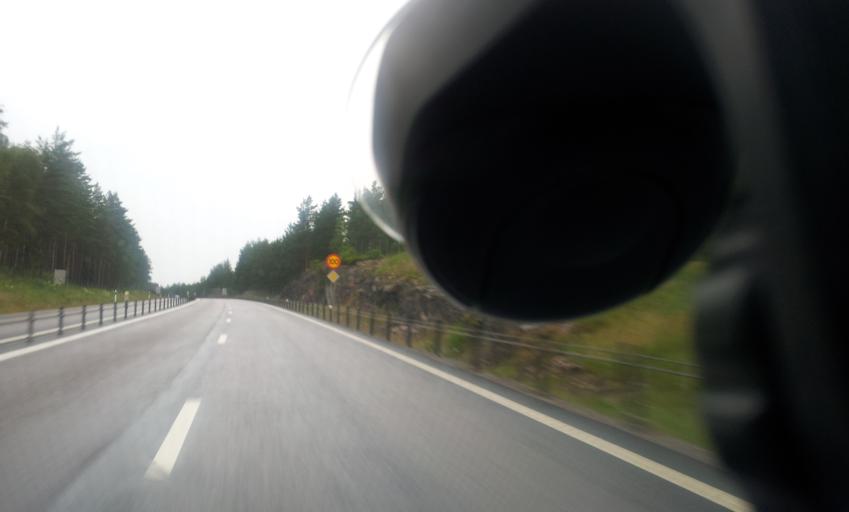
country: SE
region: OEstergoetland
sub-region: Valdemarsviks Kommun
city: Valdemarsvik
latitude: 58.2309
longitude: 16.5519
